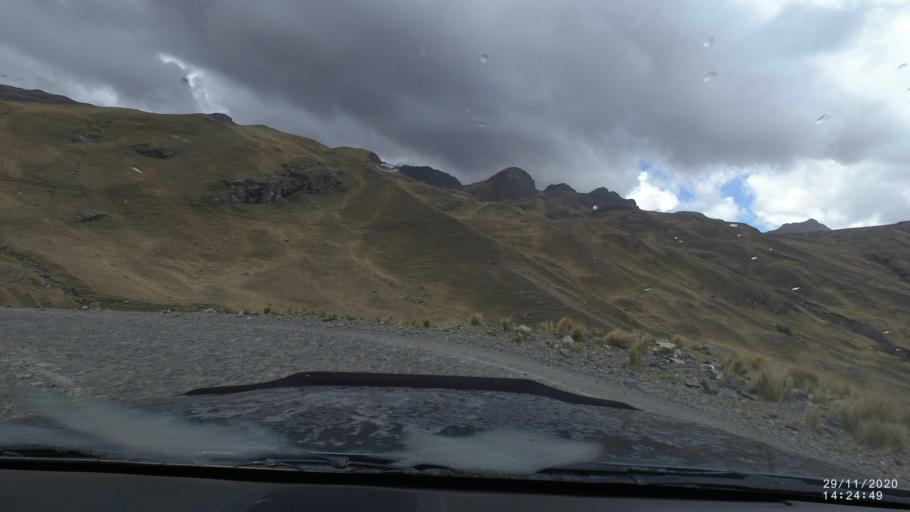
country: BO
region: Cochabamba
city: Sipe Sipe
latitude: -17.2542
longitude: -66.3770
